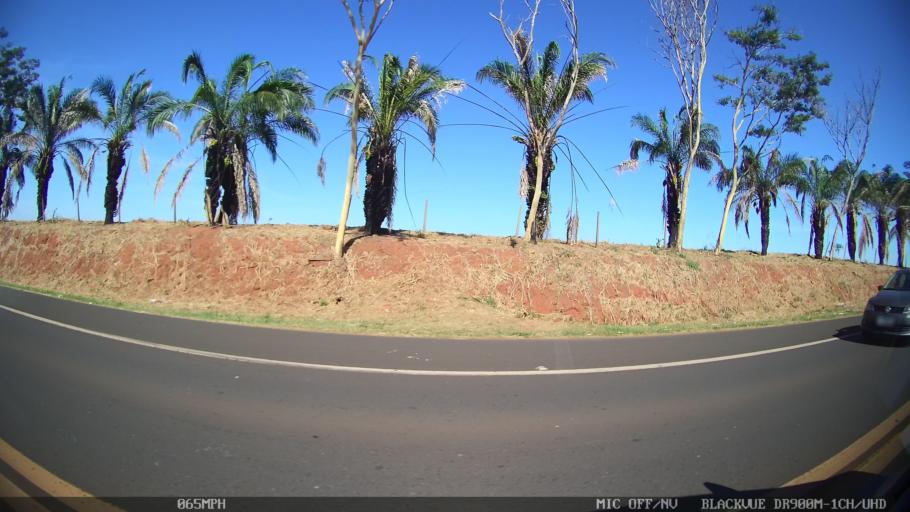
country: BR
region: Sao Paulo
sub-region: Olimpia
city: Olimpia
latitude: -20.7318
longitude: -48.8711
